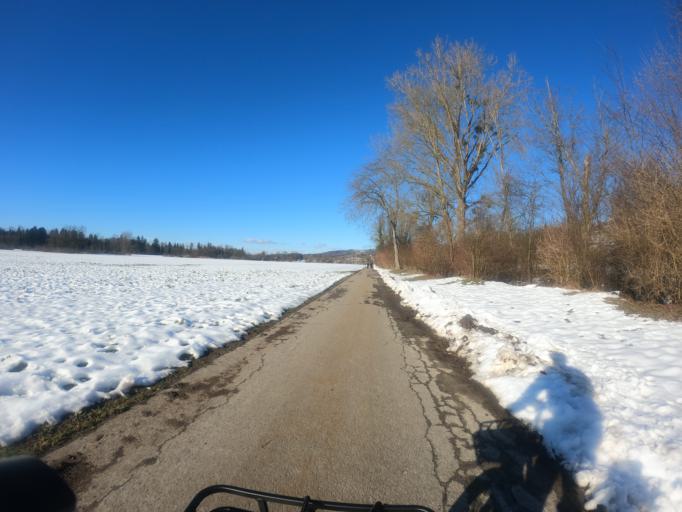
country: CH
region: Aargau
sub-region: Bezirk Bremgarten
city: Oberlunkhofen
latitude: 47.3081
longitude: 8.3860
